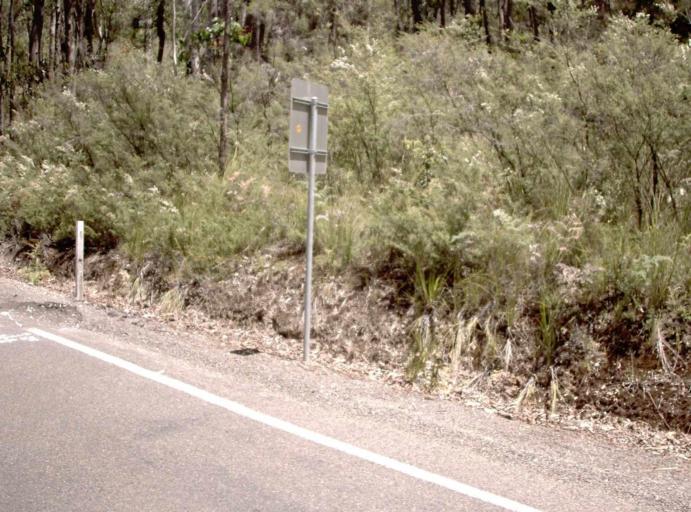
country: AU
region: Victoria
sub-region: East Gippsland
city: Lakes Entrance
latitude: -37.5786
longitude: 147.8946
